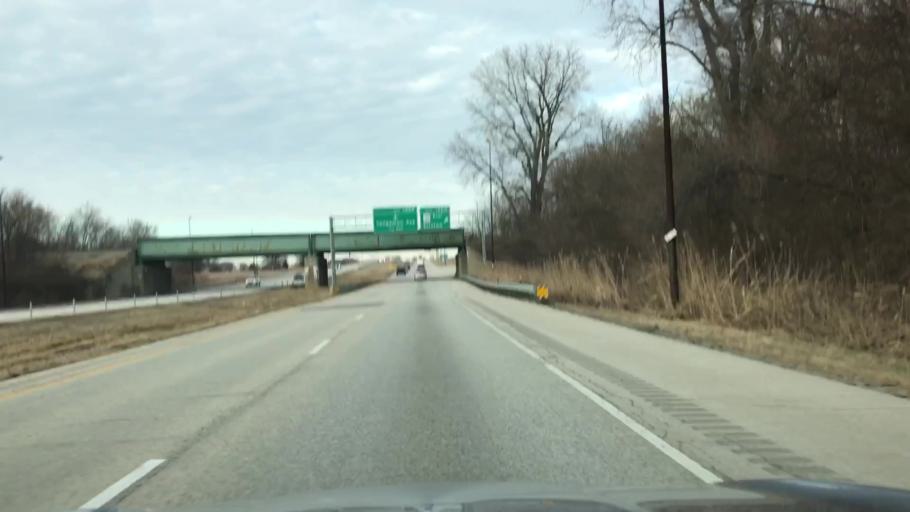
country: US
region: Illinois
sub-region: Sangamon County
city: Grandview
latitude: 39.8264
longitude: -89.5926
